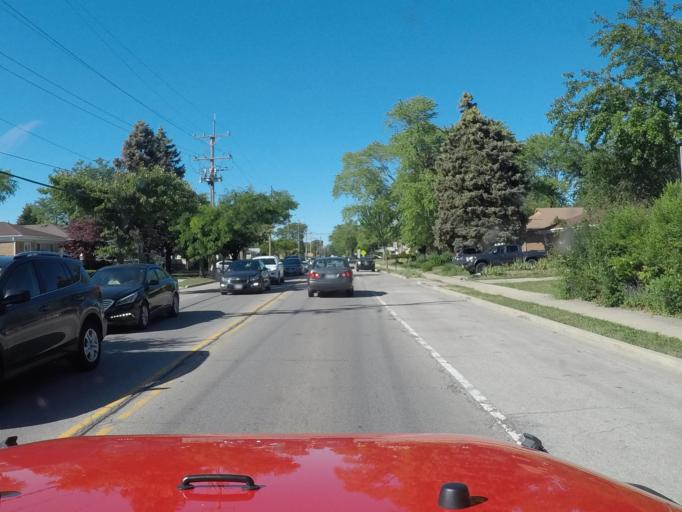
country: US
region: Illinois
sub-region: Cook County
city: Morton Grove
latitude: 42.0275
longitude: -87.7663
